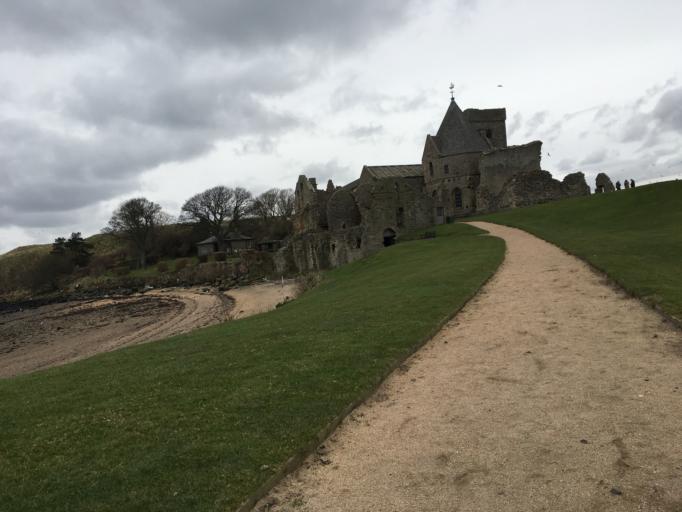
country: GB
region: Scotland
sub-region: Fife
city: Aberdour
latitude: 56.0299
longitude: -3.3002
